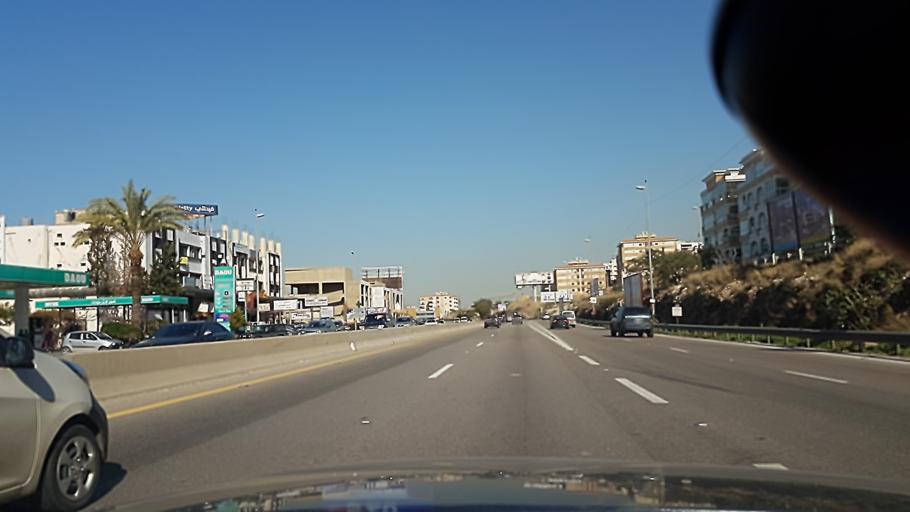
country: LB
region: Mont-Liban
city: Baabda
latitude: 33.7909
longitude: 35.4814
